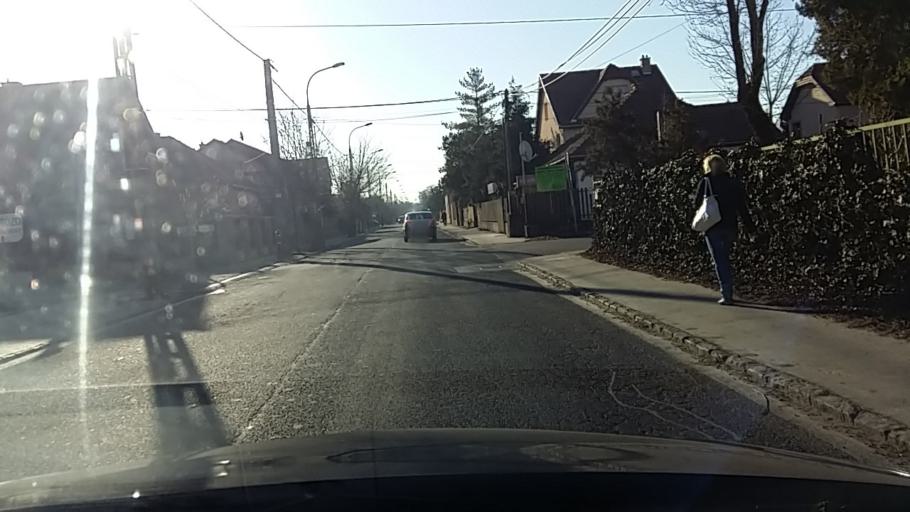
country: HU
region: Budapest
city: Budapest XVI. keruelet
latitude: 47.5273
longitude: 19.1681
